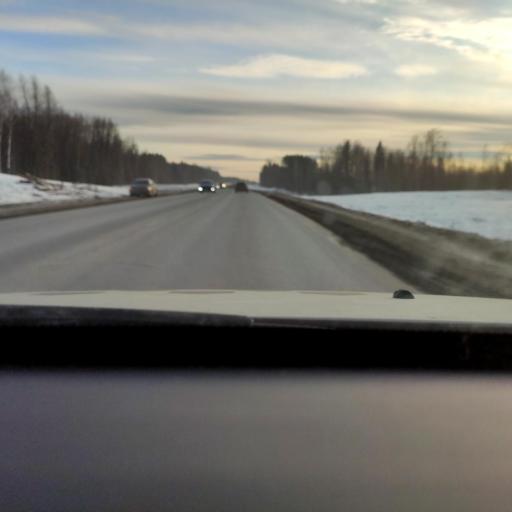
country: RU
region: Perm
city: Polazna
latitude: 58.1283
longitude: 56.4218
